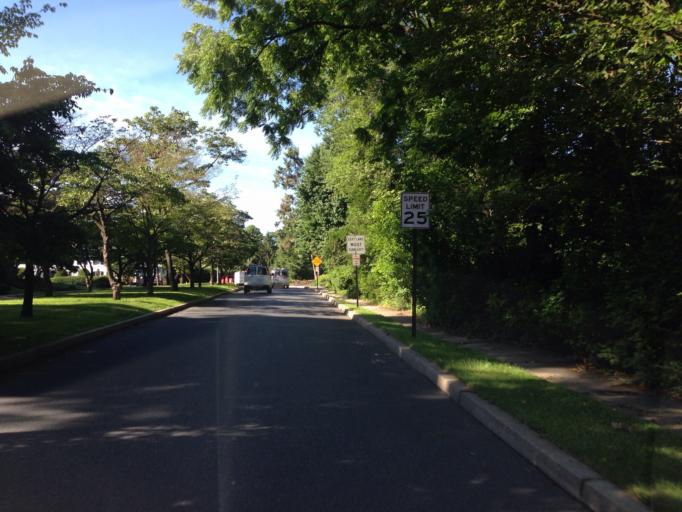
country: US
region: Pennsylvania
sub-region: Lancaster County
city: Lancaster
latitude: 40.0456
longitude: -76.3271
